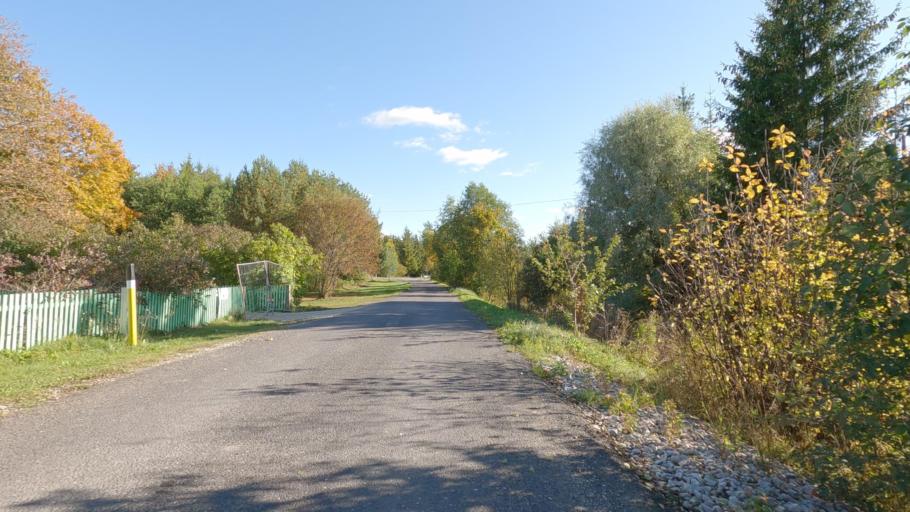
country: EE
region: Raplamaa
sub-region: Rapla vald
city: Rapla
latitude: 58.9929
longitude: 24.8360
